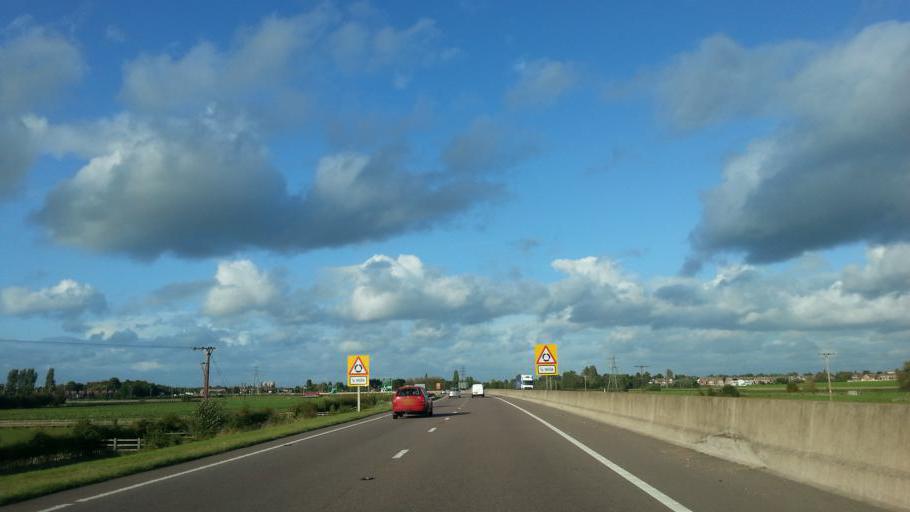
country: GB
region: England
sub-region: Nottinghamshire
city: Farndon
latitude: 53.0568
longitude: -0.8412
